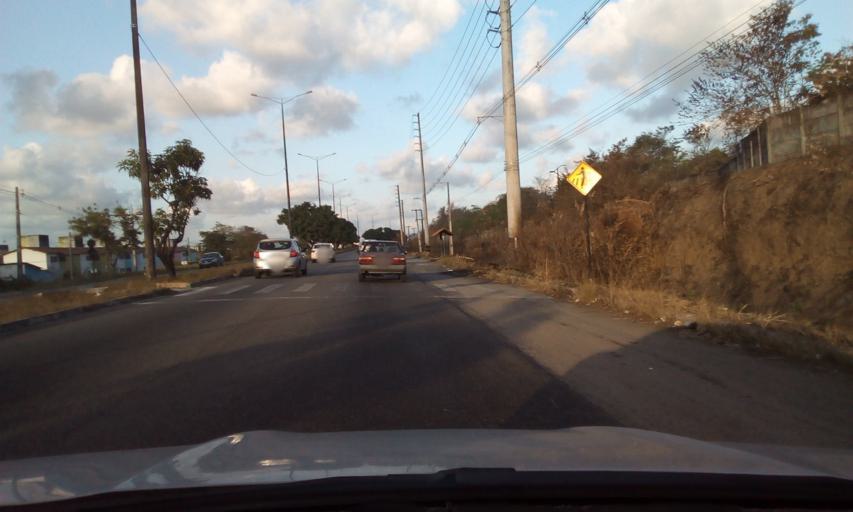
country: BR
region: Paraiba
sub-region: Bayeux
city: Bayeux
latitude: -7.1291
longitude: -34.9015
